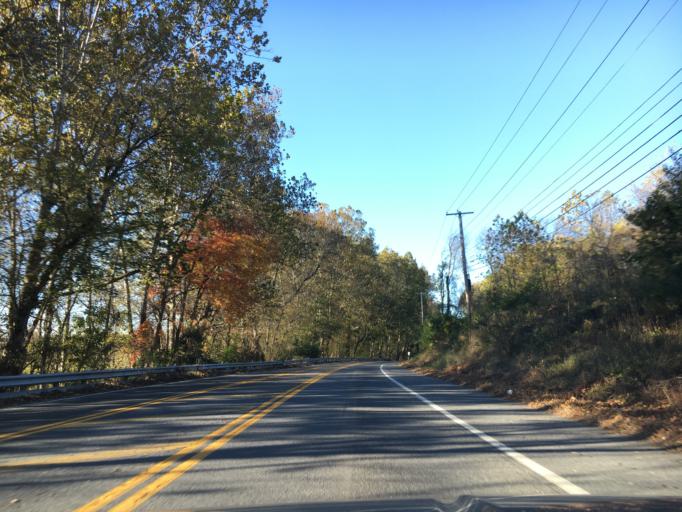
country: US
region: Pennsylvania
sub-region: Lehigh County
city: Fullerton
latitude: 40.6300
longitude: -75.4615
